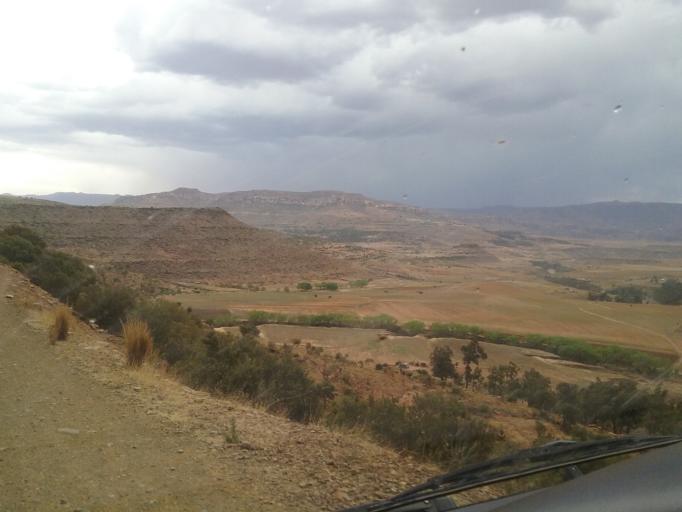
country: LS
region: Quthing
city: Quthing
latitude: -30.3031
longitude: 27.8134
